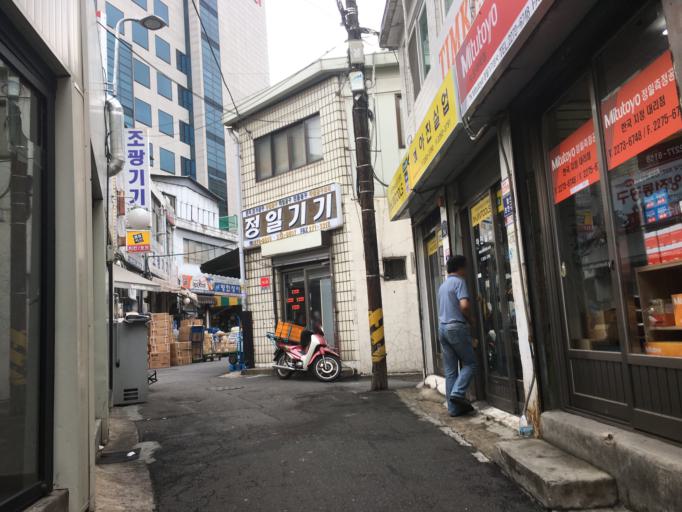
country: KR
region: Seoul
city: Seoul
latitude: 37.5675
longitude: 126.9918
